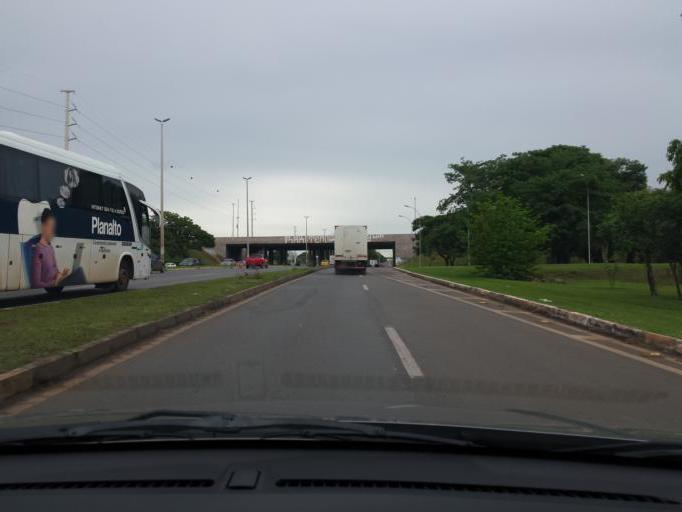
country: BR
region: Federal District
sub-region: Brasilia
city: Brasilia
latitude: -15.8423
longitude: -47.9534
